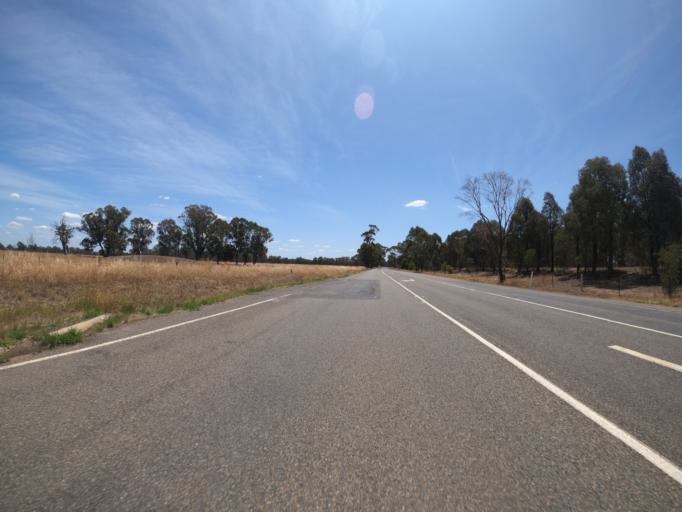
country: AU
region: Victoria
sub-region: Benalla
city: Benalla
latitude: -36.4973
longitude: 146.0198
